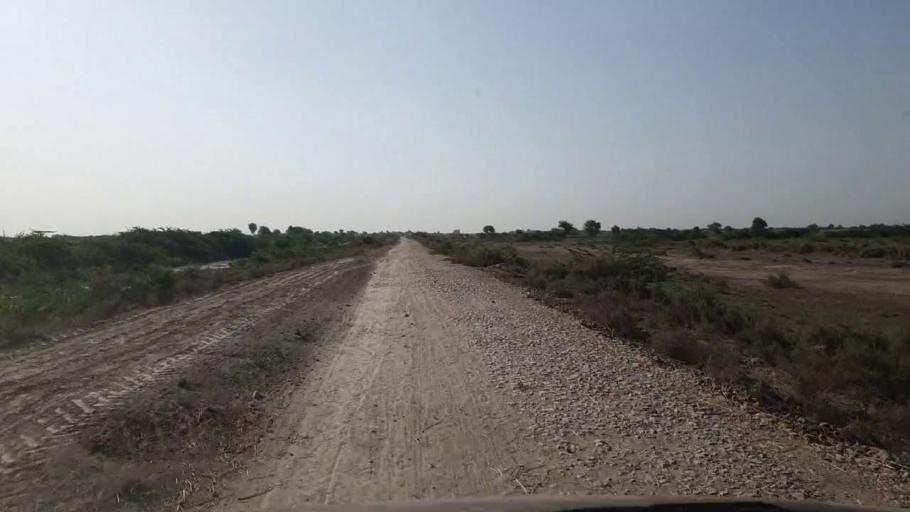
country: PK
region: Sindh
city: Kadhan
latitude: 24.6302
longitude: 69.0729
